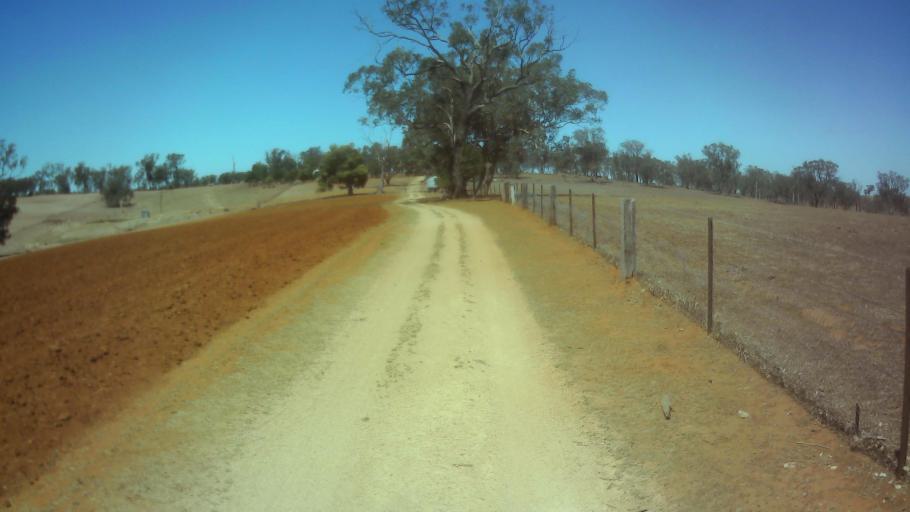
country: AU
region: New South Wales
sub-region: Cowra
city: Cowra
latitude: -33.9073
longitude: 148.5073
